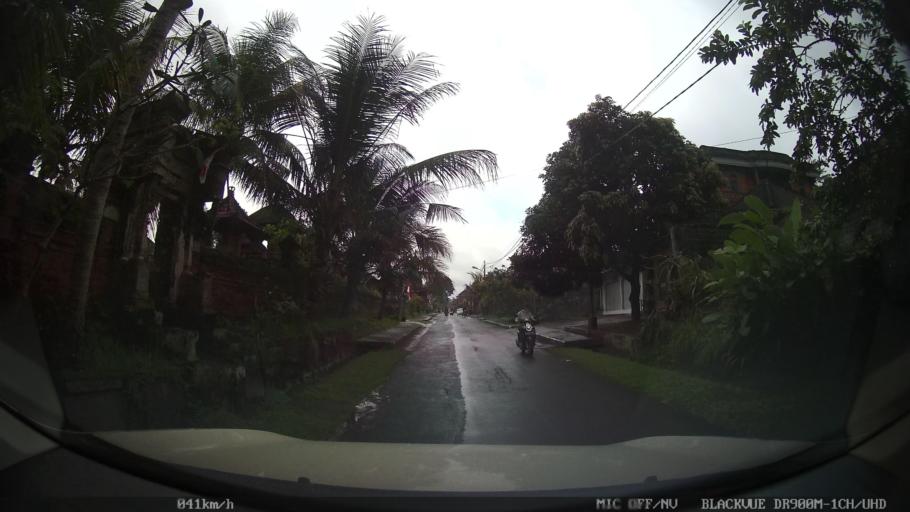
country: ID
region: Bali
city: Pegongan
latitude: -8.4919
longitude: 115.2262
